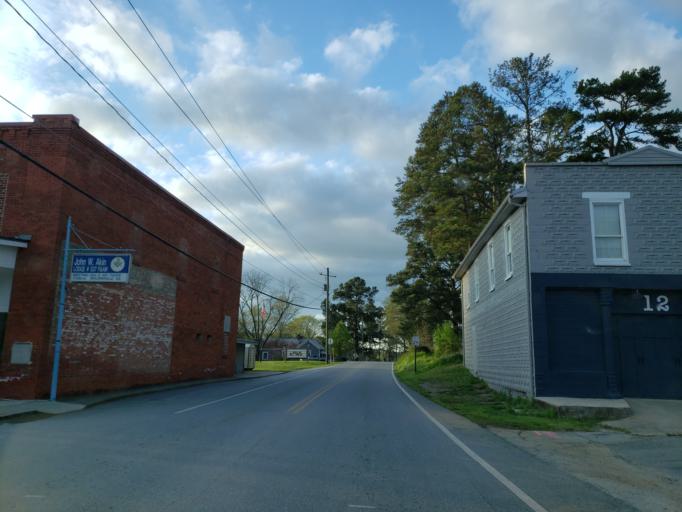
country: US
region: Georgia
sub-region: Polk County
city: Aragon
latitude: 34.0866
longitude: -84.9879
